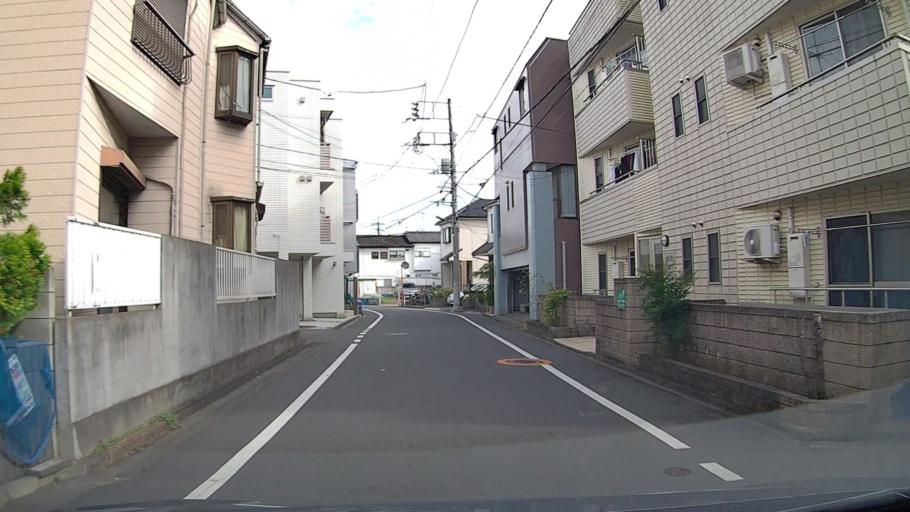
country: JP
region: Tokyo
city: Musashino
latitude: 35.7343
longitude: 139.5923
